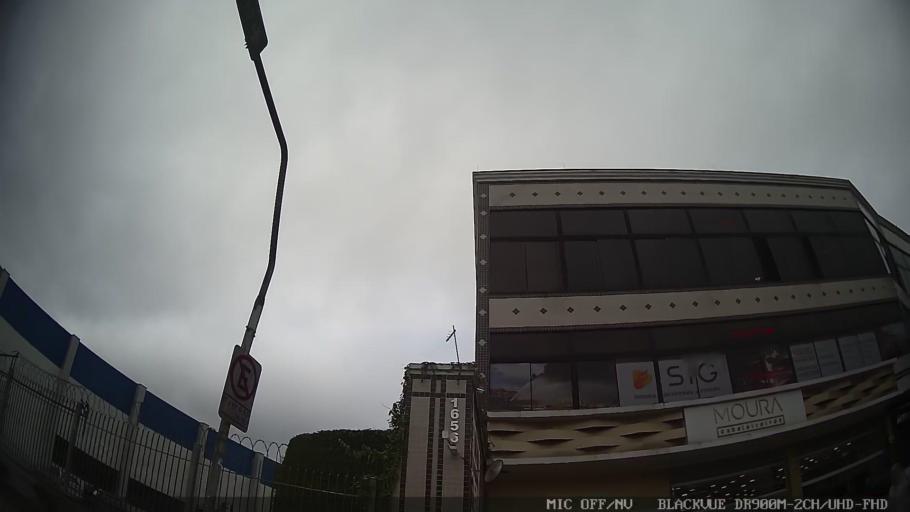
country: BR
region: Sao Paulo
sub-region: Osasco
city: Osasco
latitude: -23.4844
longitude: -46.7418
